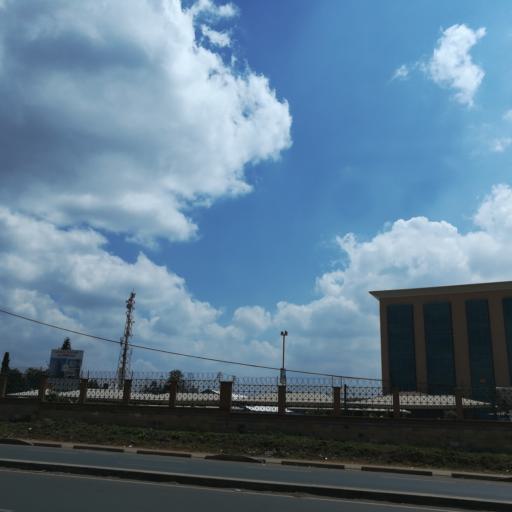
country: KE
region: Nairobi Area
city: Nairobi
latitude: -1.2978
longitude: 36.8037
